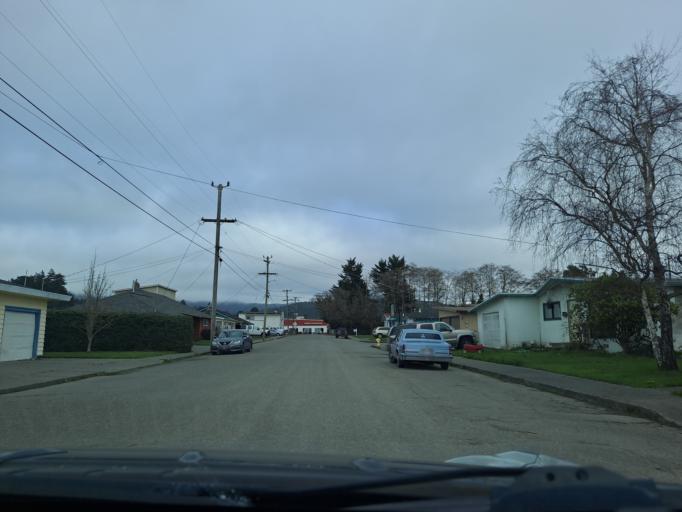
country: US
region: California
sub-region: Humboldt County
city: Fortuna
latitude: 40.5936
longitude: -124.1489
